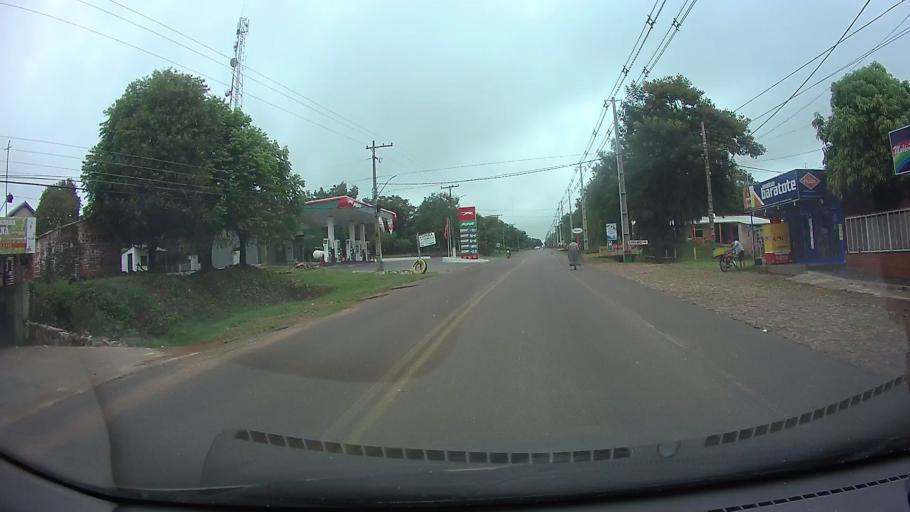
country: PY
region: Cordillera
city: Altos
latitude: -25.2689
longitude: -57.2534
